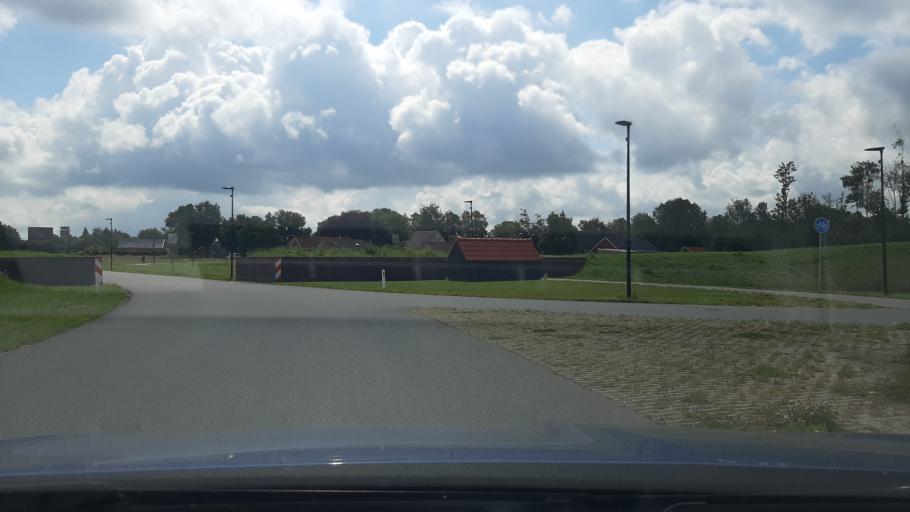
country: NL
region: Groningen
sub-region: Gemeente  Oldambt
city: Winschoten
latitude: 53.1818
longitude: 6.9627
